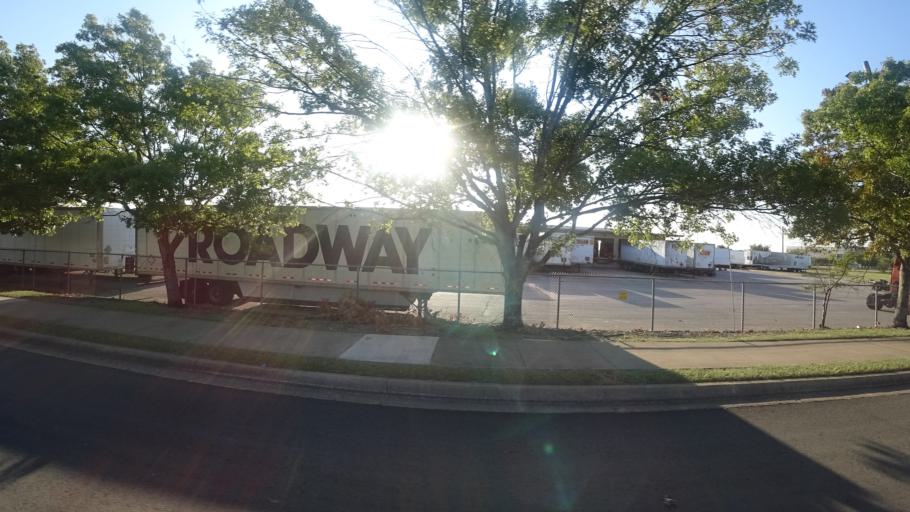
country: US
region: Texas
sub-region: Travis County
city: Manor
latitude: 30.3370
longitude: -97.6623
